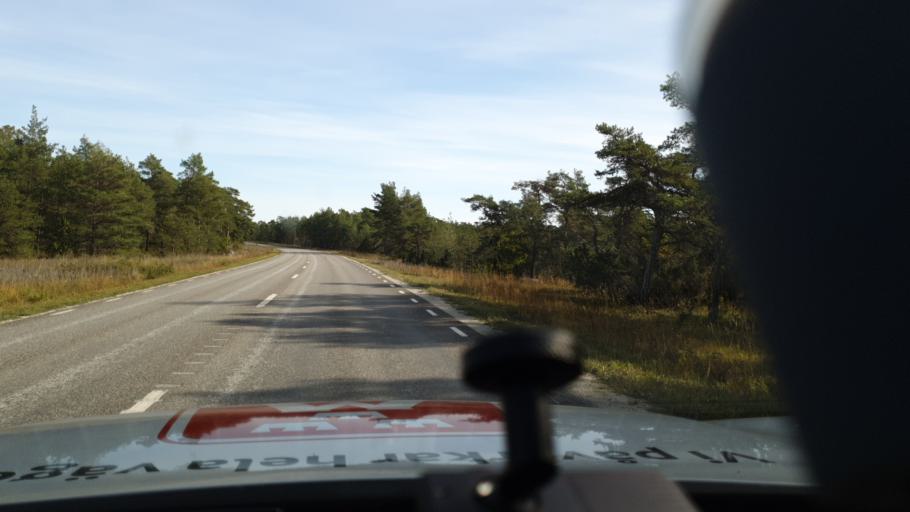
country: SE
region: Gotland
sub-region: Gotland
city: Slite
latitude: 57.8115
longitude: 18.8526
